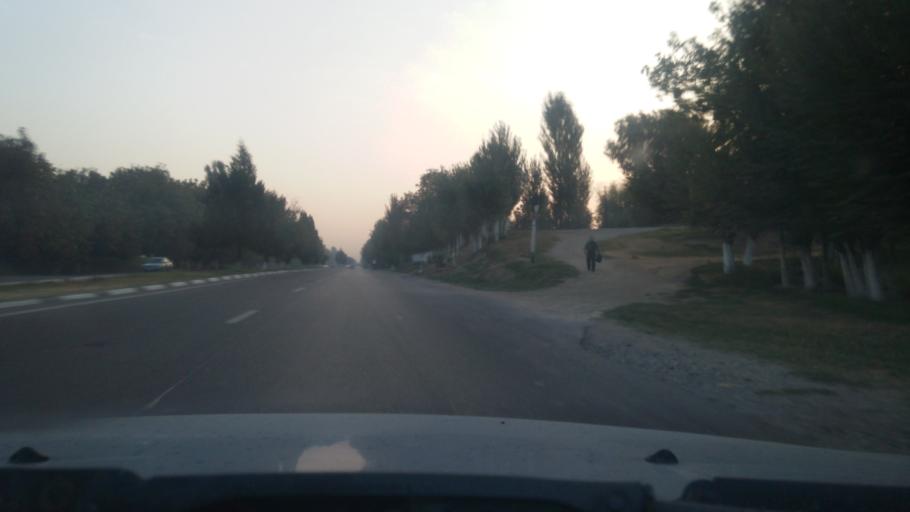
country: UZ
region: Toshkent
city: Amir Timur
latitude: 41.0588
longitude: 68.9073
